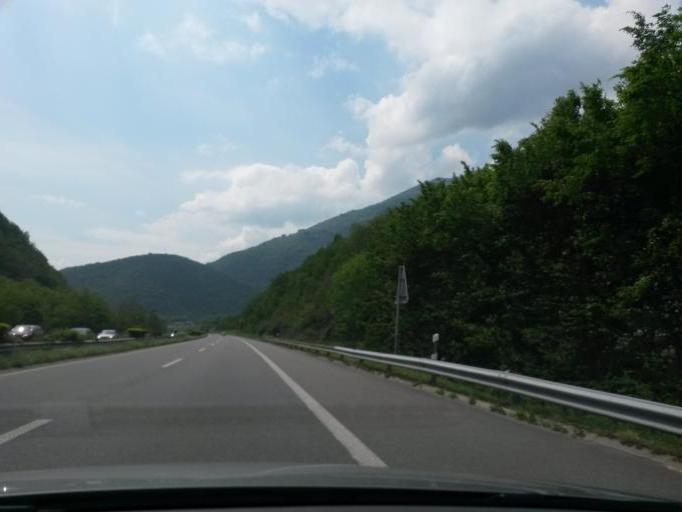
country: CH
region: Ticino
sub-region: Lugano District
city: Tesserete
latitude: 46.0910
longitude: 8.9239
